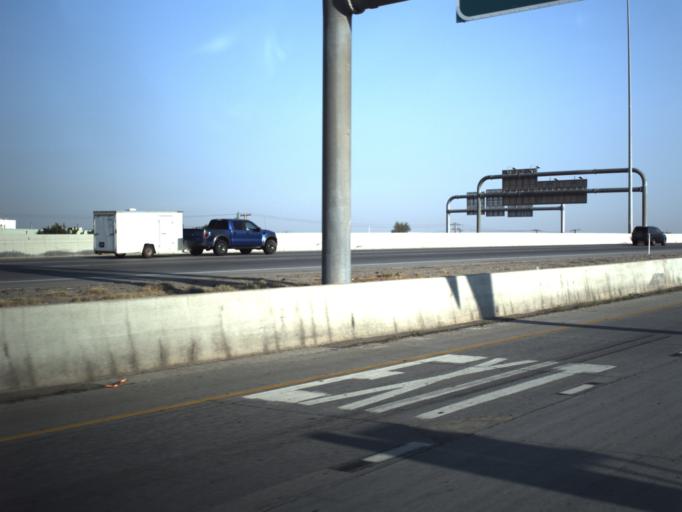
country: US
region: Utah
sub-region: Salt Lake County
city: South Salt Lake
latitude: 40.7314
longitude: -111.9040
